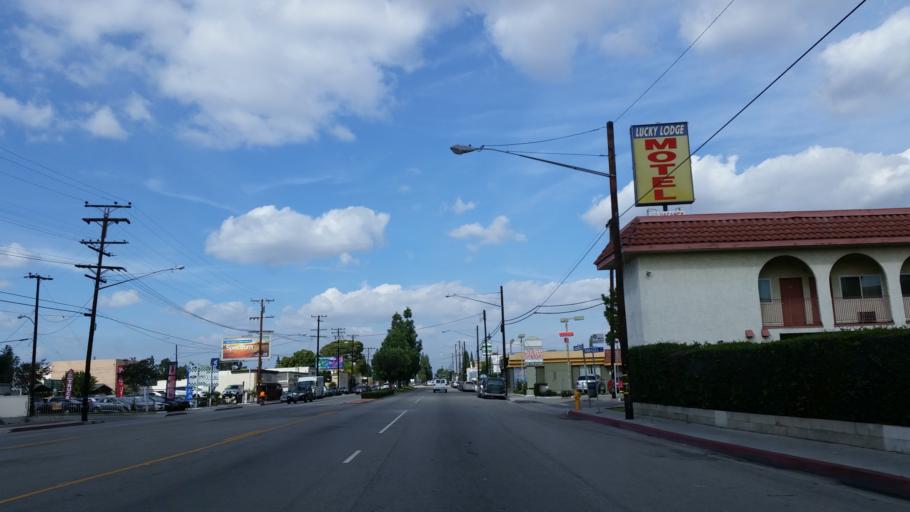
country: US
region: California
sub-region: Los Angeles County
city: Paramount
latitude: 33.8919
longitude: -118.1426
